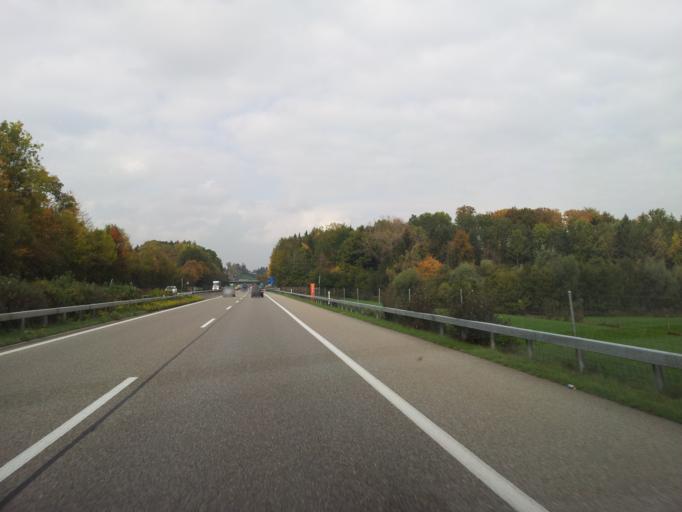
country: CH
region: Bern
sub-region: Bern-Mittelland District
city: Muri
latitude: 46.9190
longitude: 7.5089
